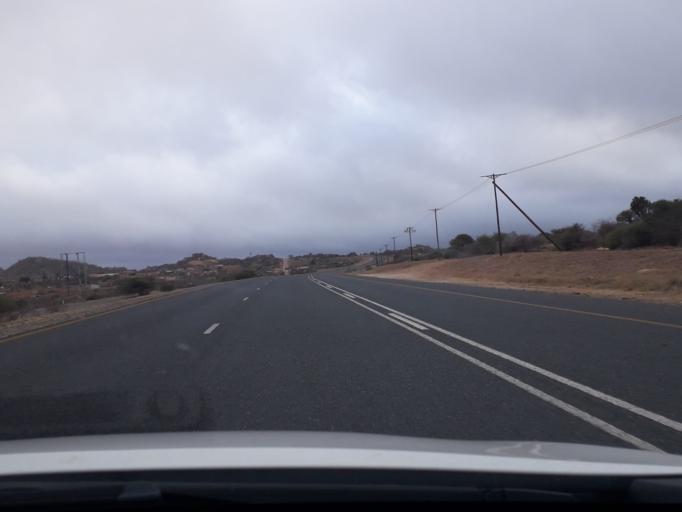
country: ZA
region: Limpopo
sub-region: Capricorn District Municipality
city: Dendron
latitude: -23.4480
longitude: 29.7410
